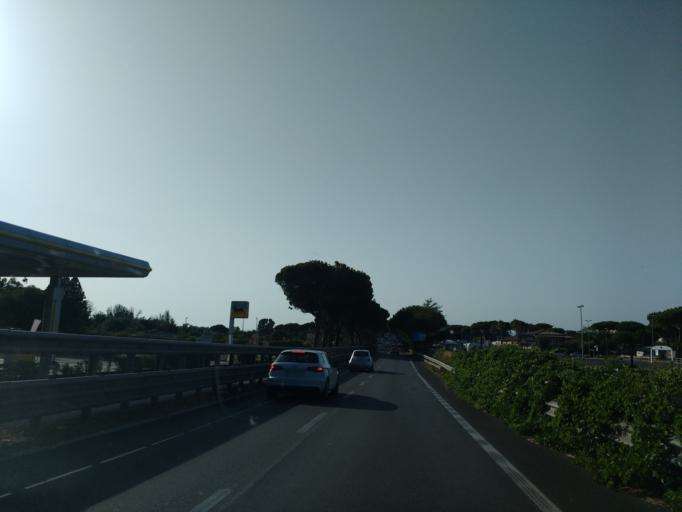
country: IT
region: Latium
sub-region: Citta metropolitana di Roma Capitale
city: Marino
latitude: 41.7732
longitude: 12.6105
